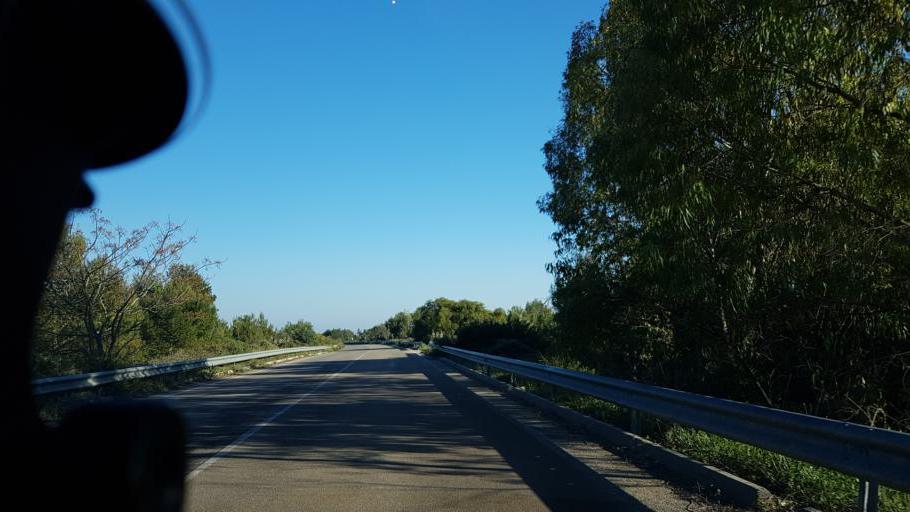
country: IT
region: Apulia
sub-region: Provincia di Lecce
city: Merine
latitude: 40.3963
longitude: 18.2532
